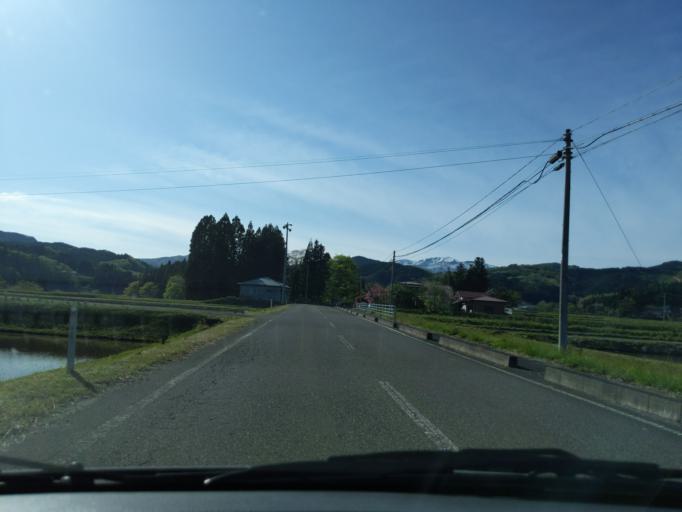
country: JP
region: Iwate
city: Ichinoseki
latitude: 38.8719
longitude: 140.8989
